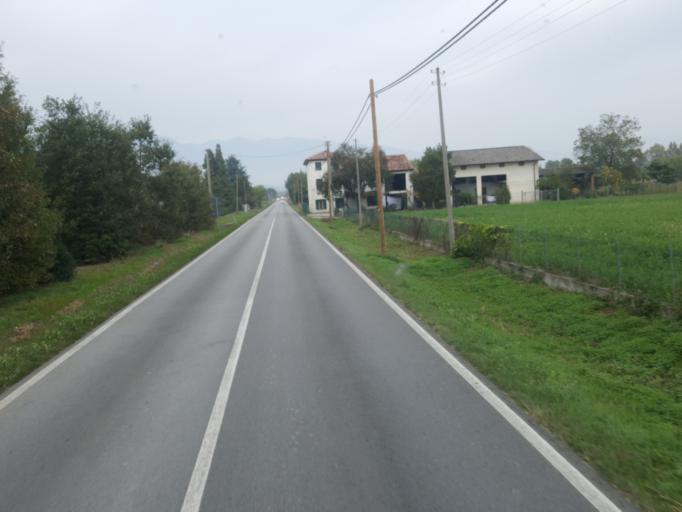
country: IT
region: Veneto
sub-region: Provincia di Treviso
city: Loria Bessica
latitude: 45.7445
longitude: 11.8662
